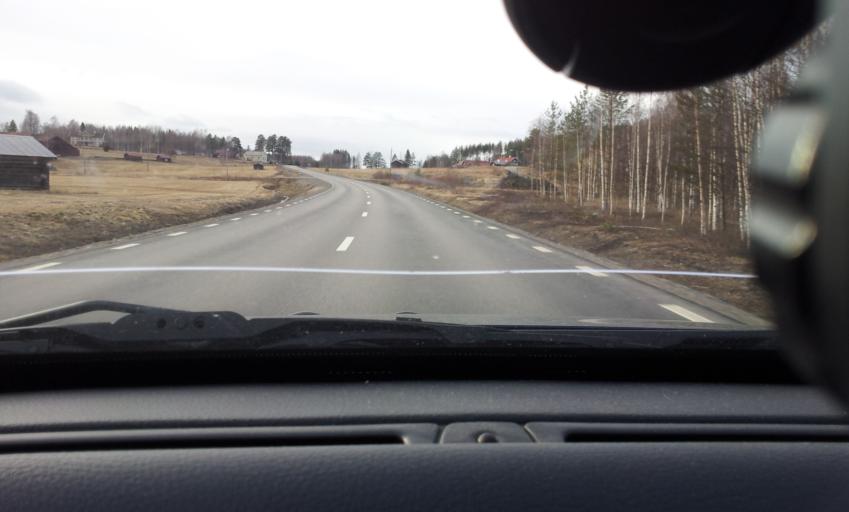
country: SE
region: Gaevleborg
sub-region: Ljusdals Kommun
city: Farila
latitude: 61.8621
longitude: 15.7403
